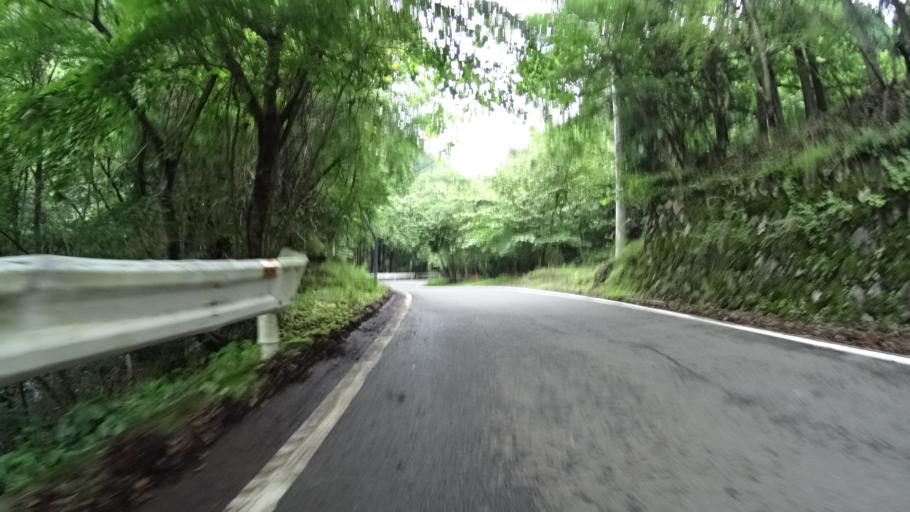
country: JP
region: Kanagawa
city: Hadano
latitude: 35.4384
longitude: 139.2109
